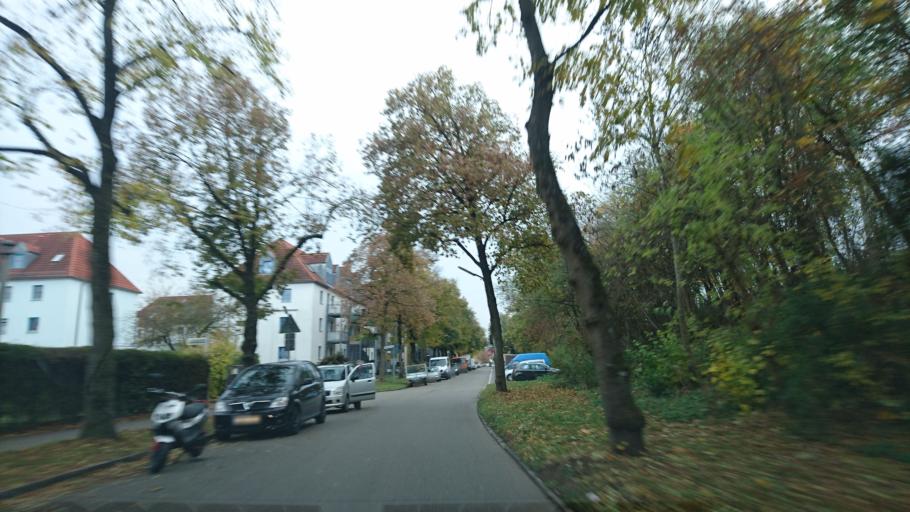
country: DE
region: Bavaria
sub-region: Swabia
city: Augsburg
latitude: 48.3958
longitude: 10.8842
